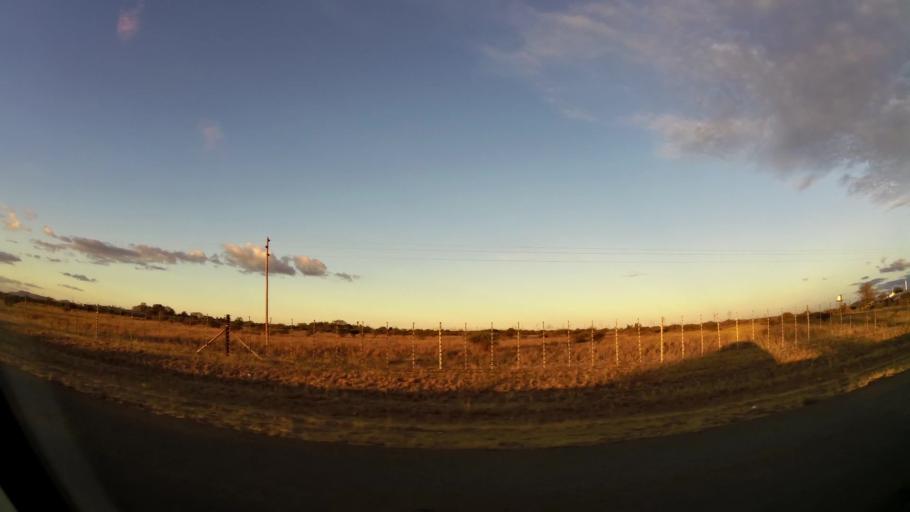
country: ZA
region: Limpopo
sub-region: Capricorn District Municipality
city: Polokwane
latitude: -23.8224
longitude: 29.4819
